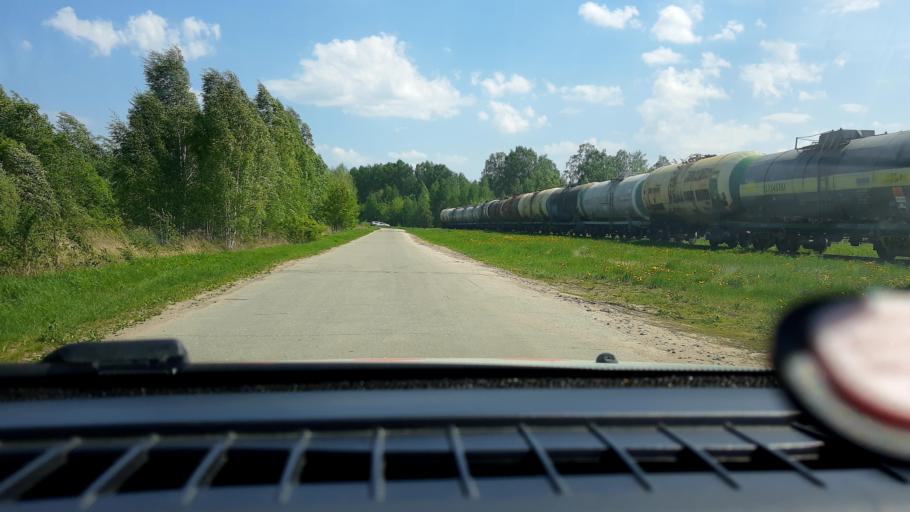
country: RU
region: Nizjnij Novgorod
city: Kstovo
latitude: 56.1467
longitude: 44.1186
